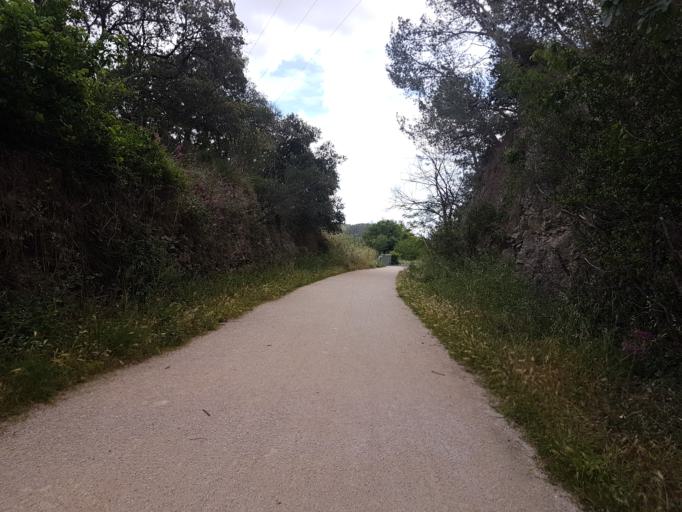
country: FR
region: Languedoc-Roussillon
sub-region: Departement du Gard
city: Beaucaire
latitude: 43.8258
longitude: 4.6263
